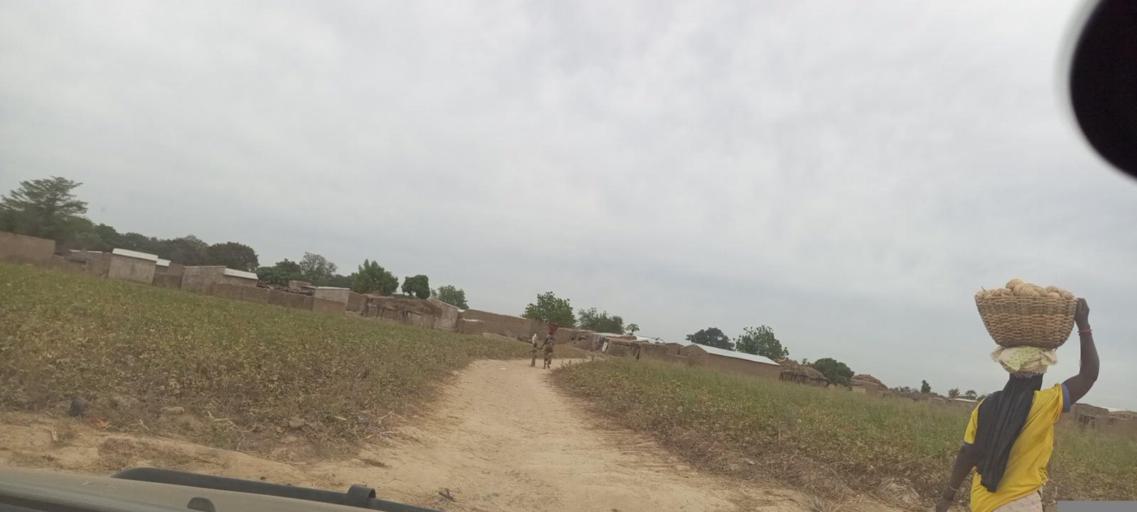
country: ML
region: Koulikoro
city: Kati
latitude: 12.7478
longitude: -8.3593
